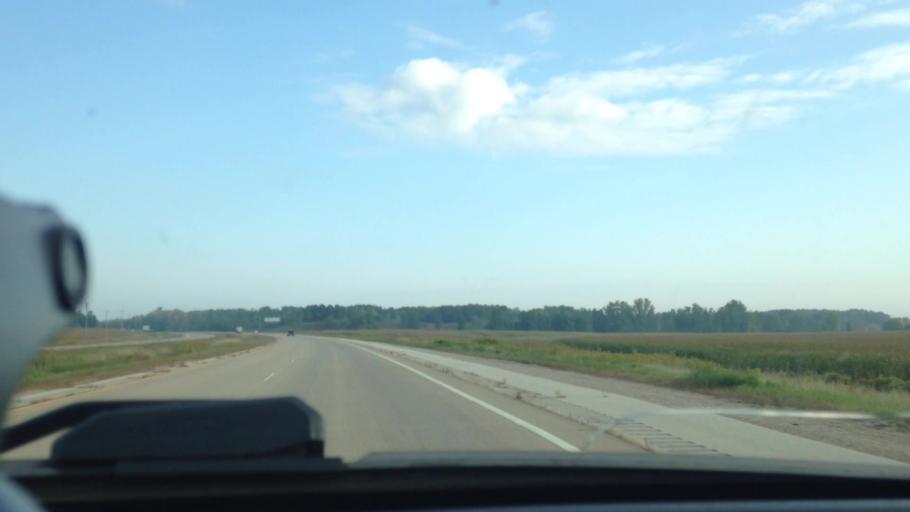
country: US
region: Wisconsin
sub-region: Oconto County
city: Oconto Falls
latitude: 44.9635
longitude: -88.0349
